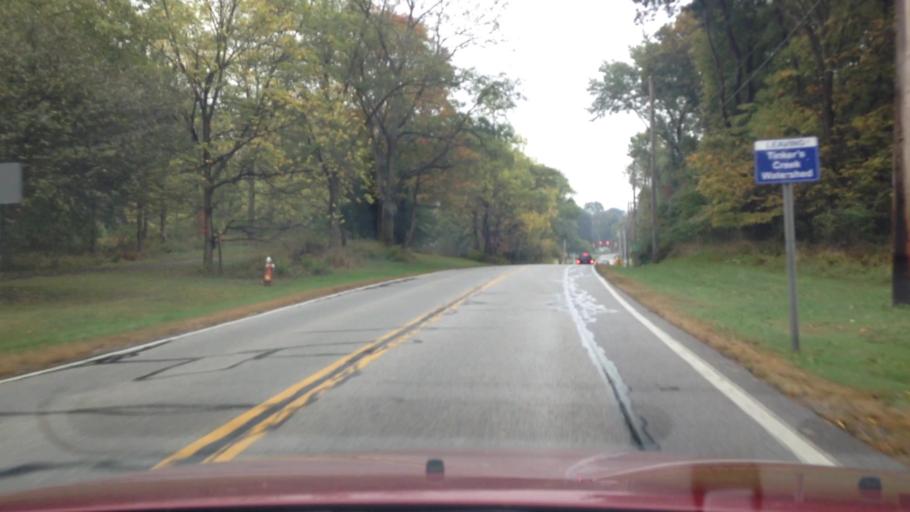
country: US
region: Ohio
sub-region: Cuyahoga County
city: Walton Hills
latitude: 41.3602
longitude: -81.5656
